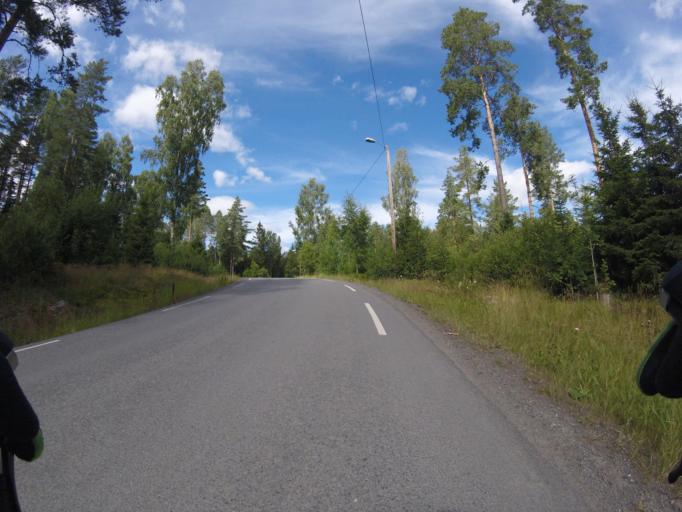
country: NO
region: Akershus
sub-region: Lorenskog
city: Kjenn
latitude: 59.8939
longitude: 10.9754
